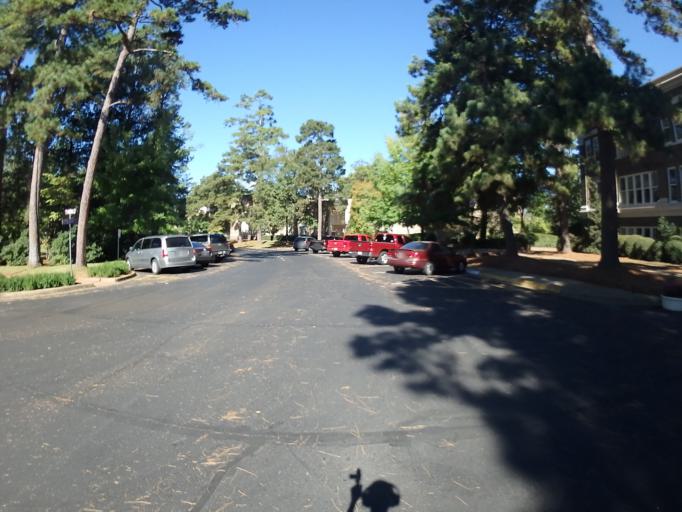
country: US
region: Texas
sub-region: Nacogdoches County
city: Nacogdoches
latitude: 31.6219
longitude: -94.6500
